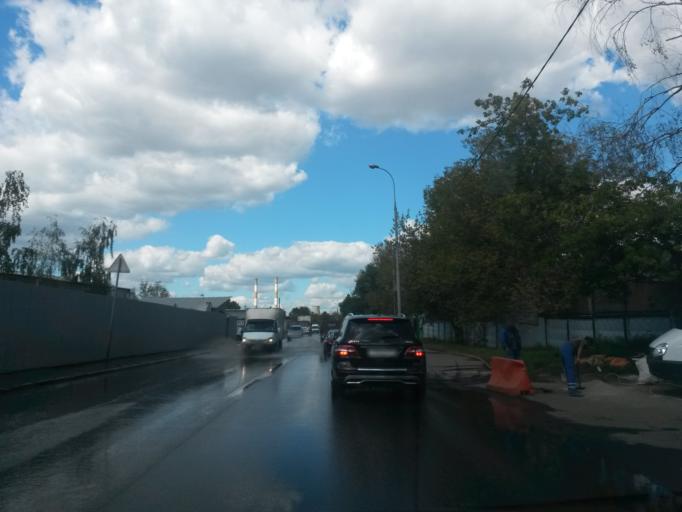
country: RU
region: Moskovskaya
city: Kozhukhovo
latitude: 55.7044
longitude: 37.7026
